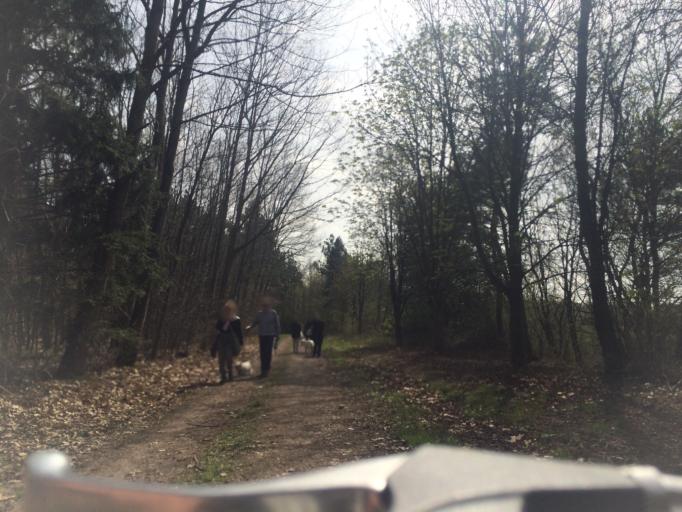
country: DE
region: Hesse
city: Morfelden-Walldorf
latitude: 49.9913
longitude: 8.5967
